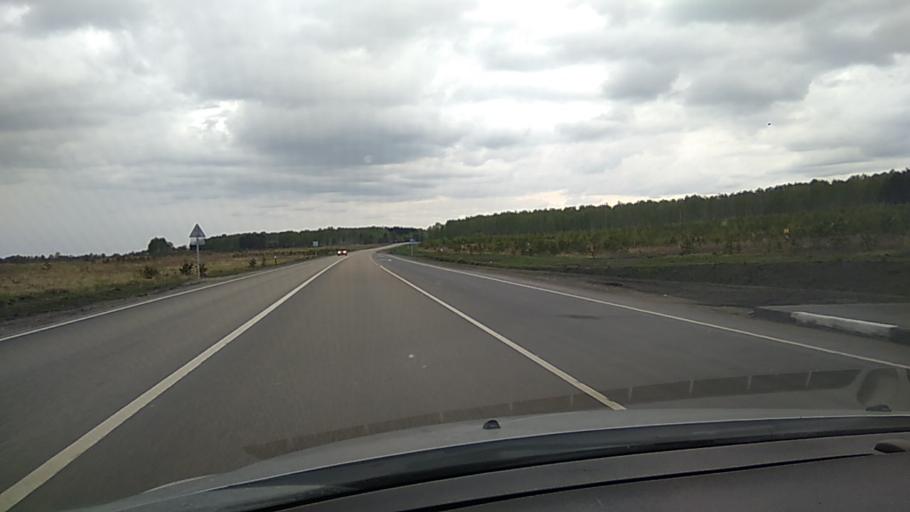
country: RU
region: Kurgan
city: Kataysk
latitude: 56.2965
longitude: 62.4048
